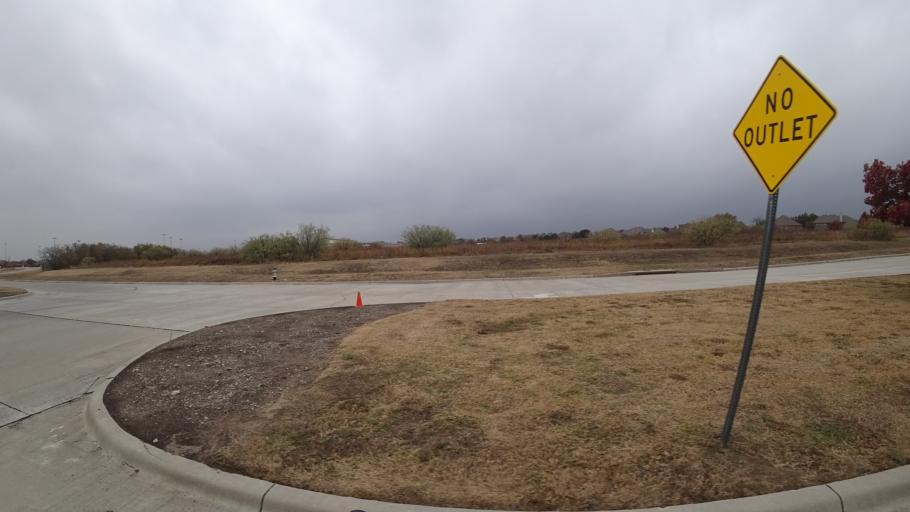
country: US
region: Texas
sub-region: Denton County
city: Lewisville
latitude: 33.0390
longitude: -96.9299
